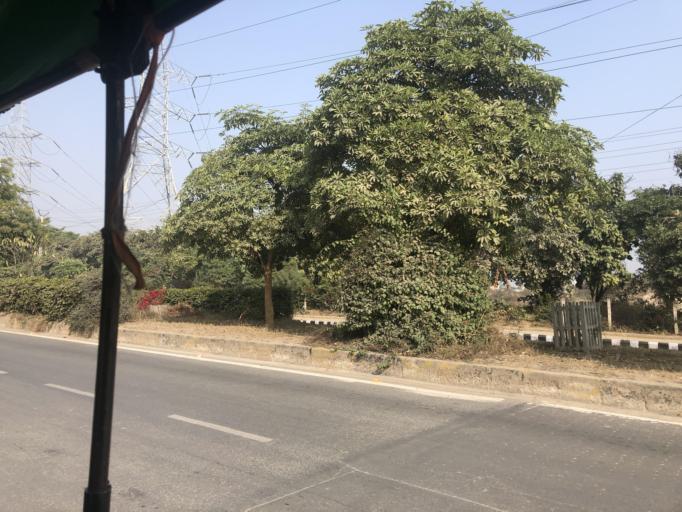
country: IN
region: Haryana
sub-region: Gurgaon
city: Gurgaon
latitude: 28.4438
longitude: 77.0834
